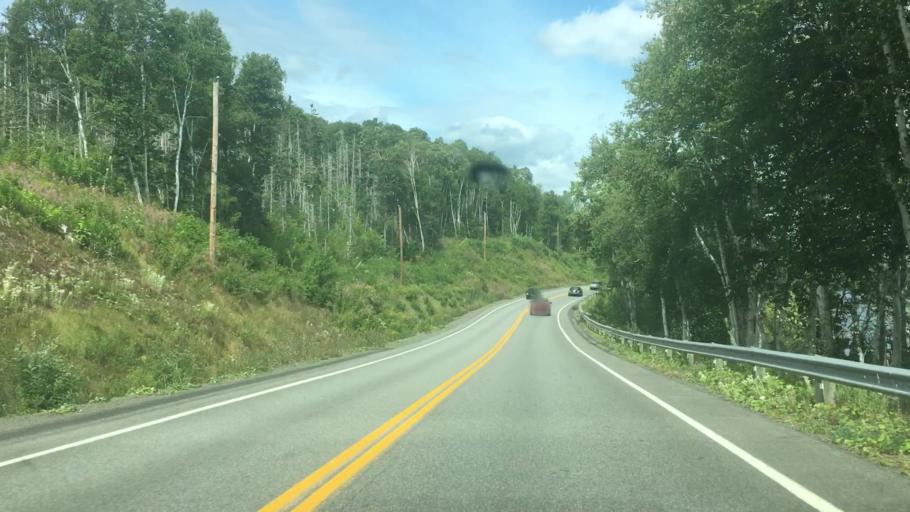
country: CA
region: Nova Scotia
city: Sydney Mines
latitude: 46.2692
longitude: -60.6090
